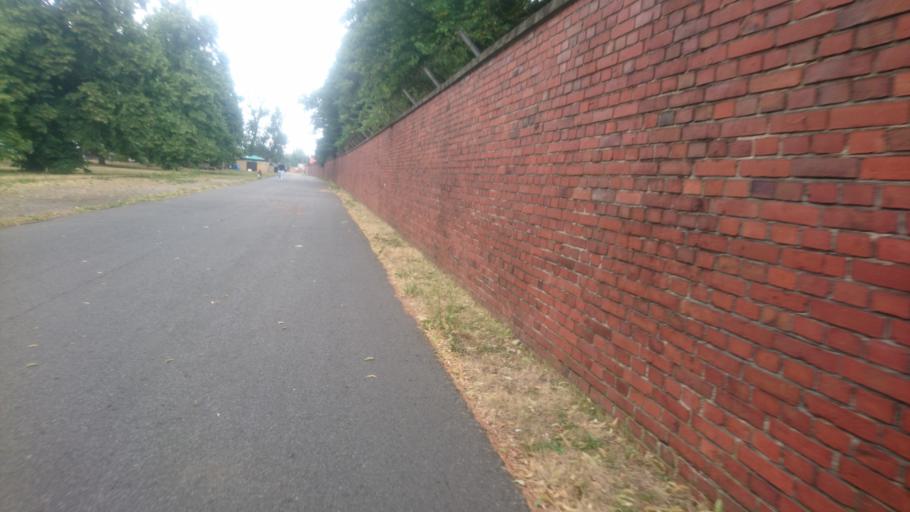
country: DE
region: Berlin
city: Tempelhof Bezirk
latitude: 52.4801
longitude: 13.4087
